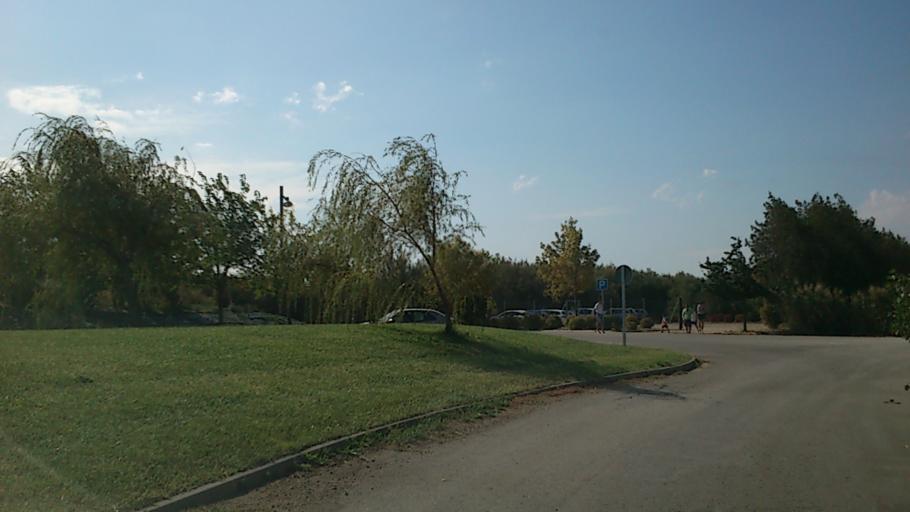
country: ES
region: Aragon
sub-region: Provincia de Zaragoza
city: Puebla de Alfinden
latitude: 41.6082
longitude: -0.7580
